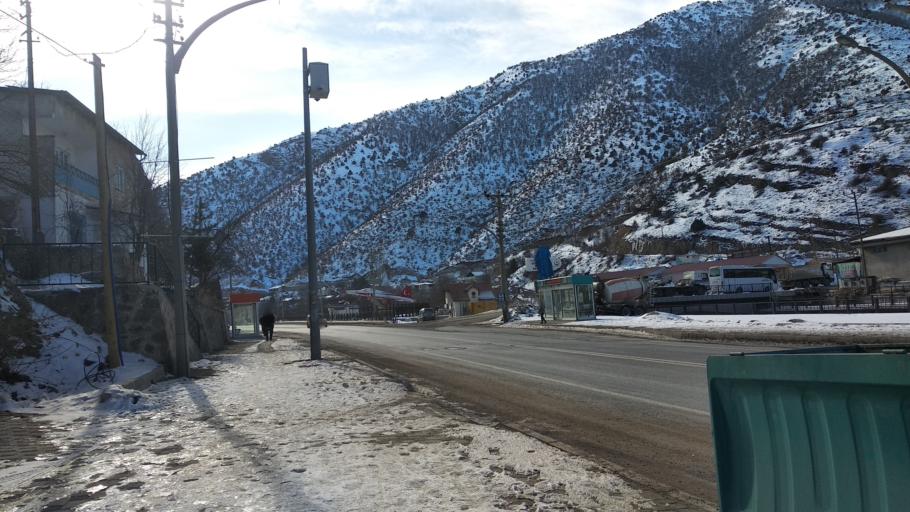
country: TR
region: Gumushane
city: Gumushkhane
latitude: 40.4409
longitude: 39.5039
